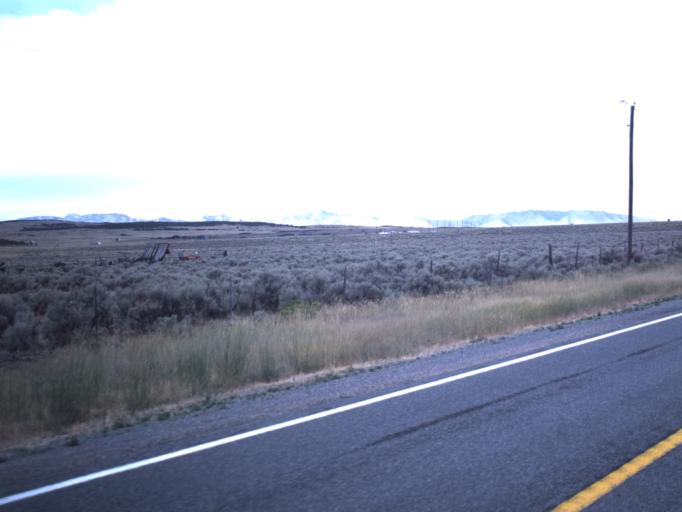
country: US
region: Utah
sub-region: Beaver County
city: Beaver
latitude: 38.6074
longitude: -112.5914
